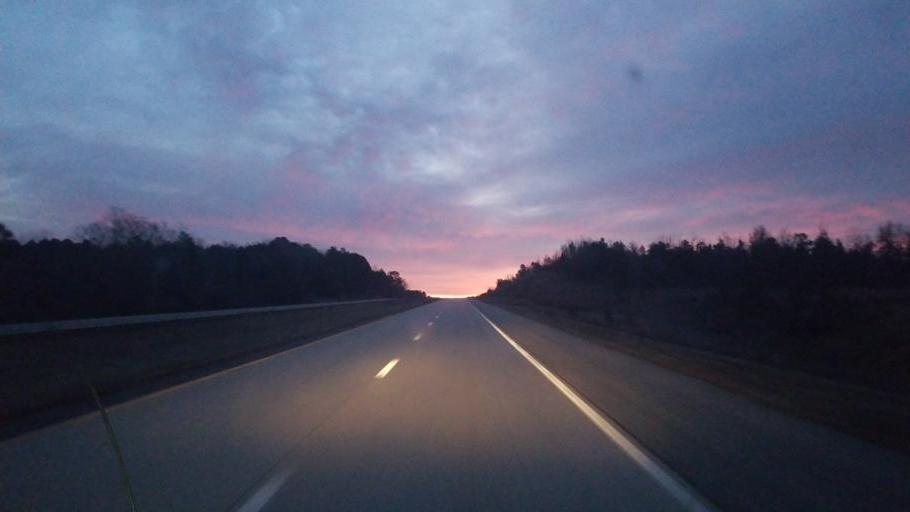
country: US
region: Missouri
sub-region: Shannon County
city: Winona
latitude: 36.9983
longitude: -91.4071
